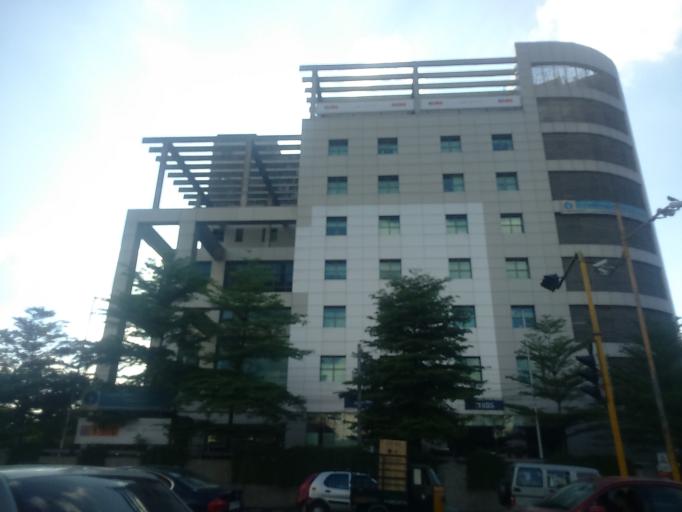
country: IN
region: Tamil Nadu
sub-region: Chennai
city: Chetput
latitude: 13.0691
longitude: 80.2425
